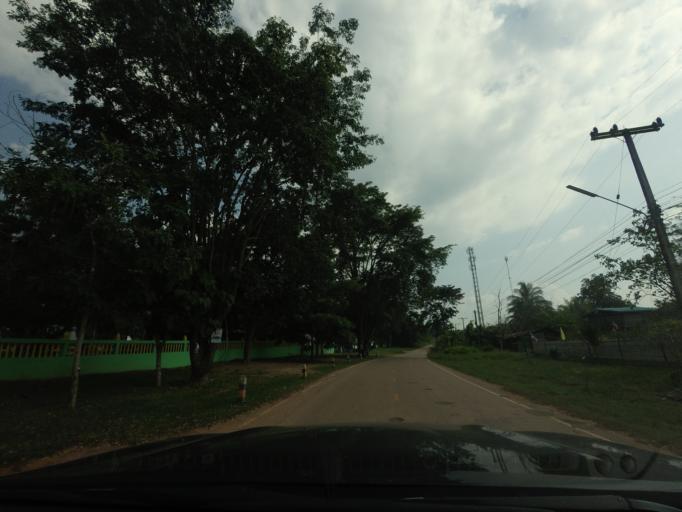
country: TH
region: Phitsanulok
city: Nakhon Thai
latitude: 17.0491
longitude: 100.9095
